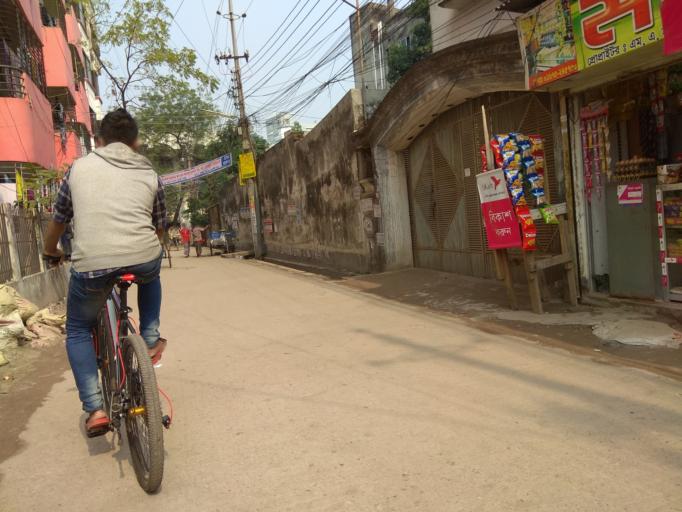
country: BD
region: Dhaka
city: Tungi
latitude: 23.8616
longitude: 90.3905
